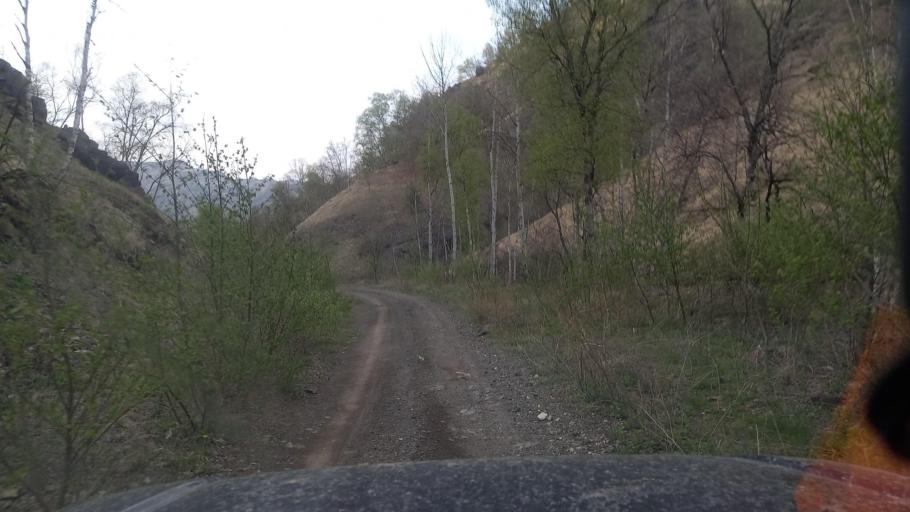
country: RU
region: Kabardino-Balkariya
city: Kamennomostskoye
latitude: 43.7100
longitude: 42.8469
